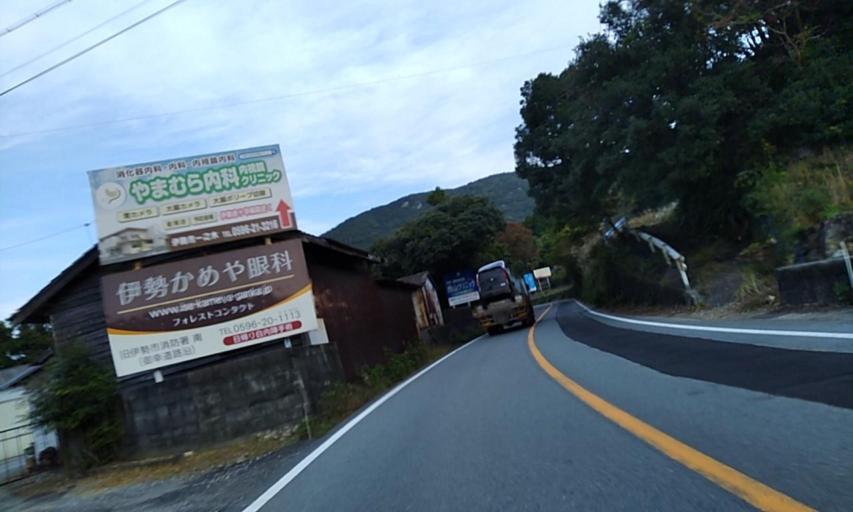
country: JP
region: Mie
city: Toba
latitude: 34.3920
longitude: 136.7872
